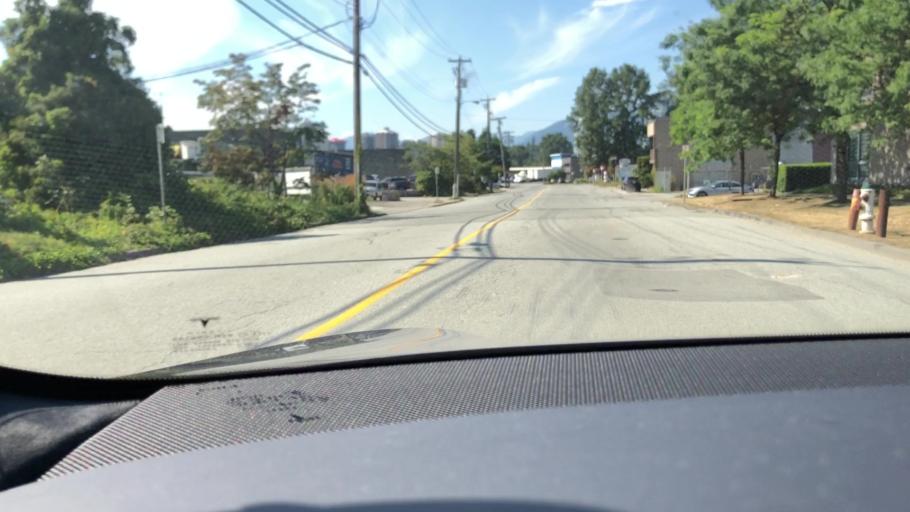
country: CA
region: British Columbia
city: Burnaby
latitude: 49.2562
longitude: -122.9765
